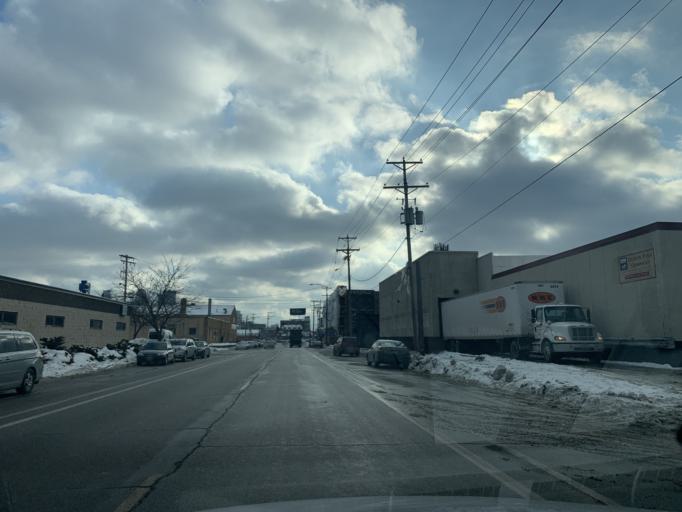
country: US
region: Minnesota
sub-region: Hennepin County
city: Minneapolis
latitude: 45.0010
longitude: -93.2802
